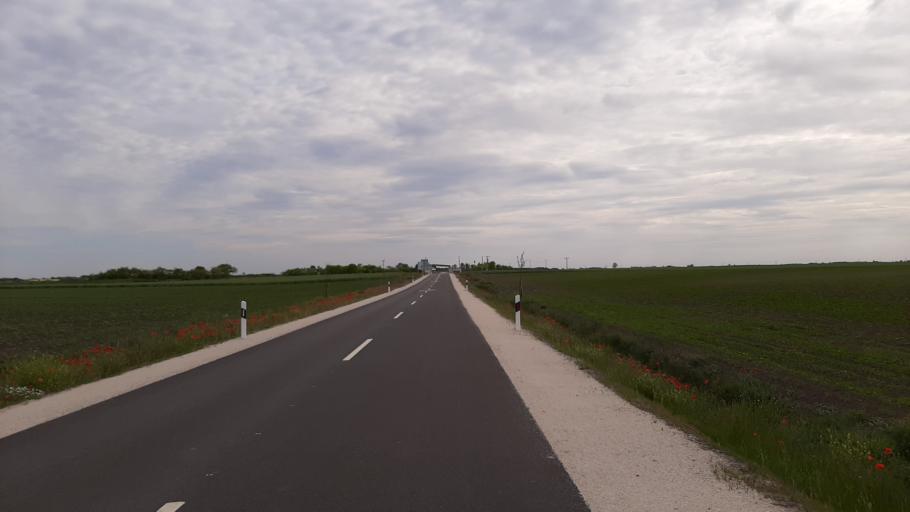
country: RO
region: Timis
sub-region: Comuna Beba Veche
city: Beba Veche
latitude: 46.1295
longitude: 20.2666
